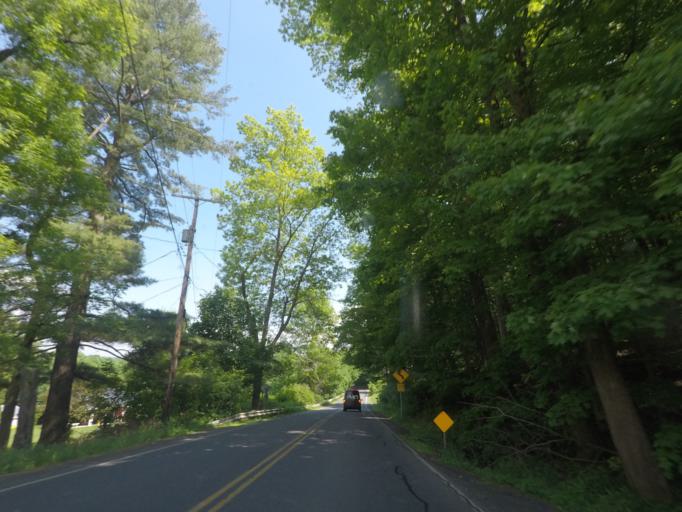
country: US
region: New York
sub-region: Dutchess County
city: Pine Plains
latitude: 41.9653
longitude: -73.5264
